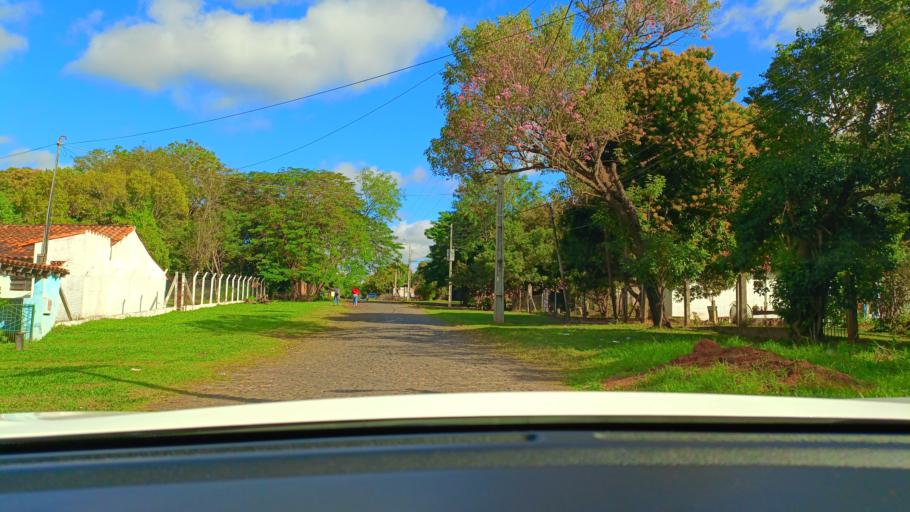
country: PY
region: San Pedro
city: Guayaybi
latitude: -24.6571
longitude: -56.4434
